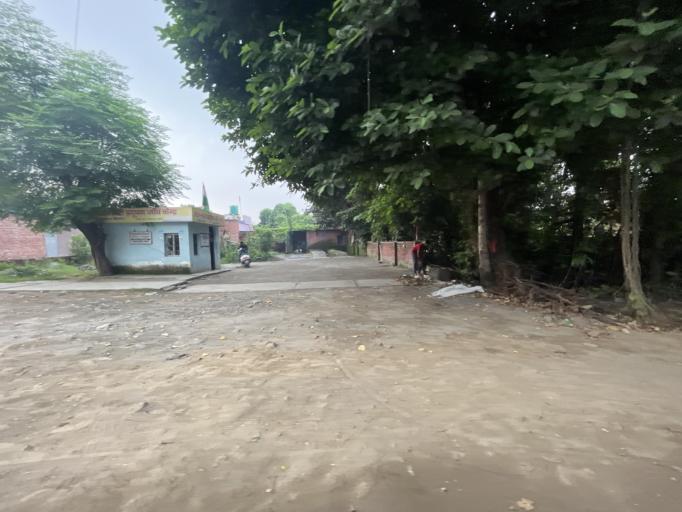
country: IN
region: Uttarakhand
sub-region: Naini Tal
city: Haldwani
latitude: 29.1966
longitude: 79.5118
